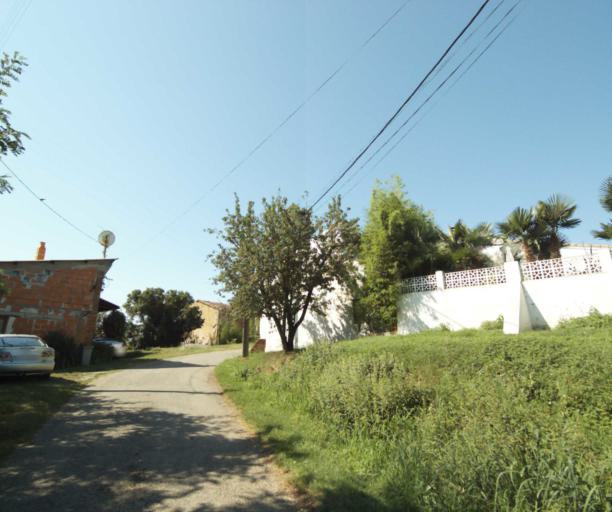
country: FR
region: Midi-Pyrenees
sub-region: Departement de l'Ariege
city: Lezat-sur-Leze
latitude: 43.2986
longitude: 1.3234
